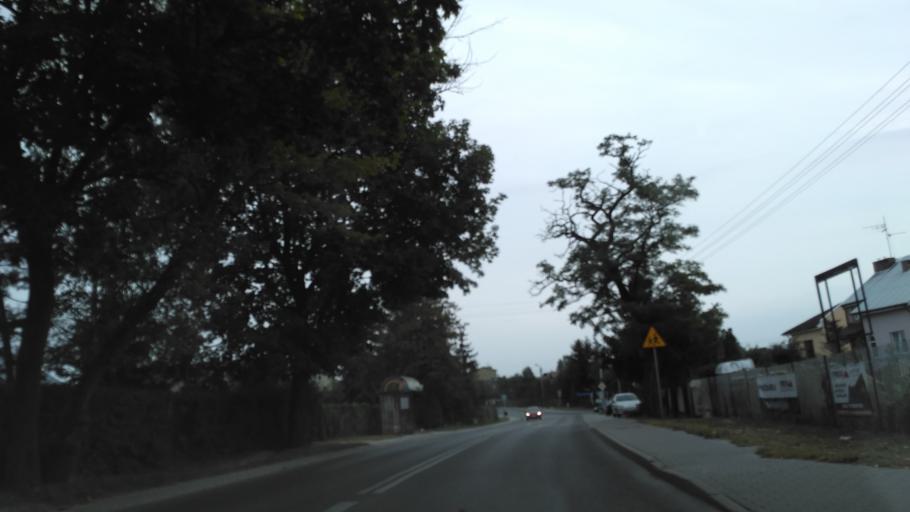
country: PL
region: Lublin Voivodeship
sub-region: Powiat lubelski
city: Lublin
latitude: 51.2214
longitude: 22.5886
